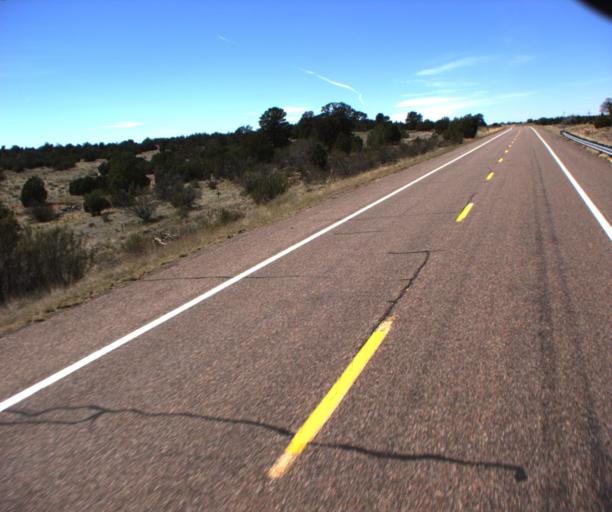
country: US
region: Arizona
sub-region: Mohave County
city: Peach Springs
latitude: 35.5111
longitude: -113.1891
